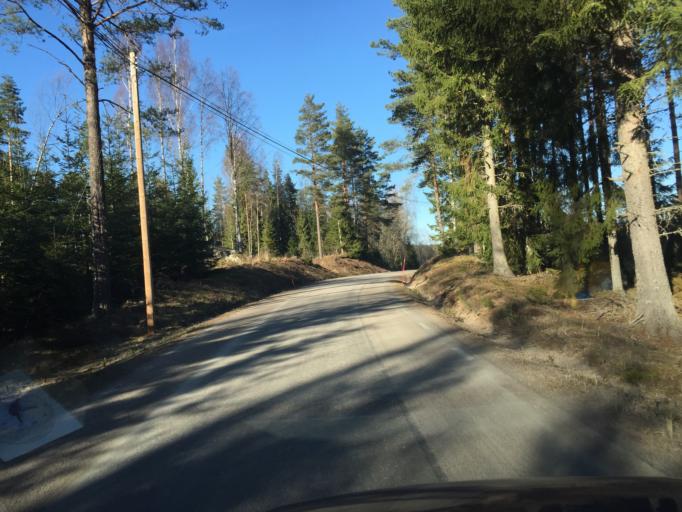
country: SE
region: Soedermanland
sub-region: Vingakers Kommun
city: Vingaker
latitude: 58.9591
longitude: 15.6727
